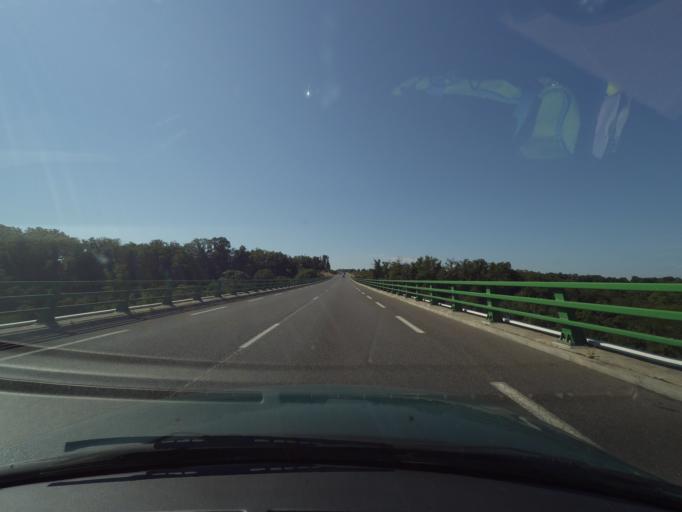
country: FR
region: Limousin
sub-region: Departement de la Haute-Vienne
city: Bellac
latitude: 46.1172
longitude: 1.0753
